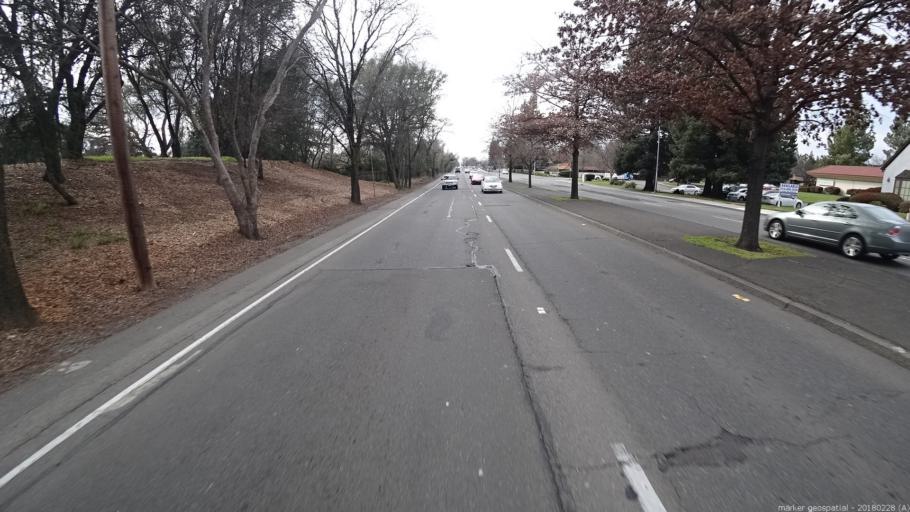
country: US
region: California
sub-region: Sacramento County
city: Fair Oaks
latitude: 38.6640
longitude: -121.2656
